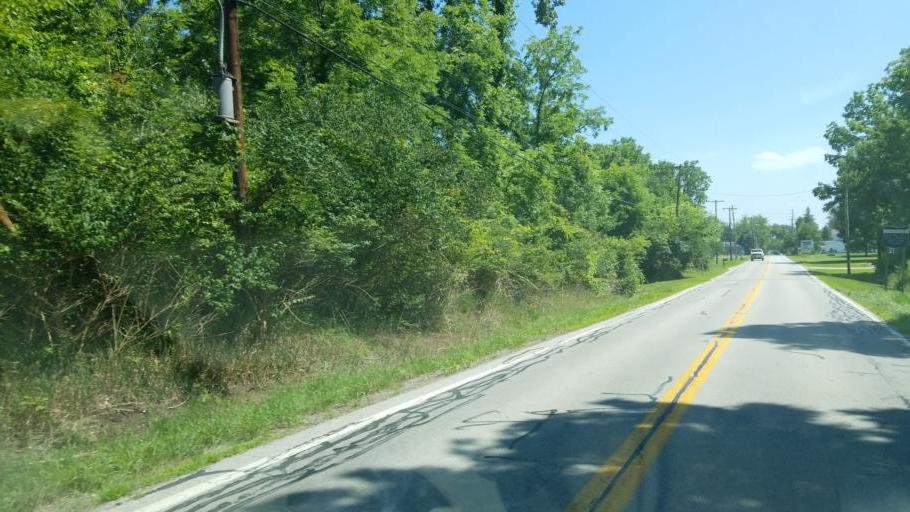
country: US
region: Ohio
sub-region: Erie County
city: Sandusky
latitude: 41.4071
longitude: -82.8122
